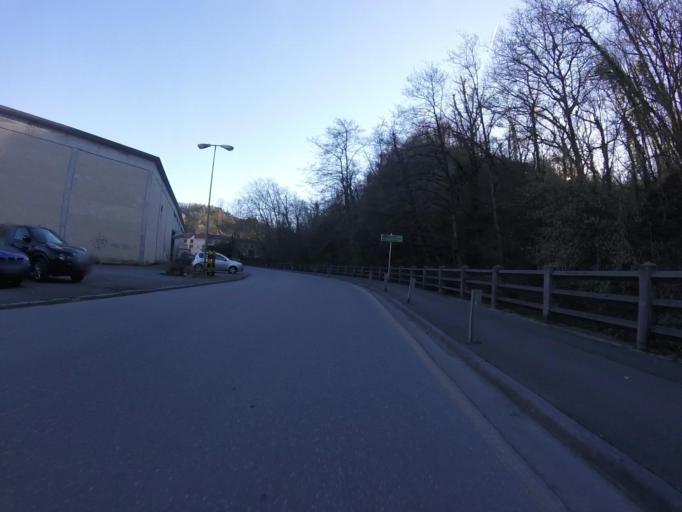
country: ES
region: Basque Country
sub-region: Provincia de Guipuzcoa
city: Errenteria
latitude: 43.2941
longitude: -1.8849
